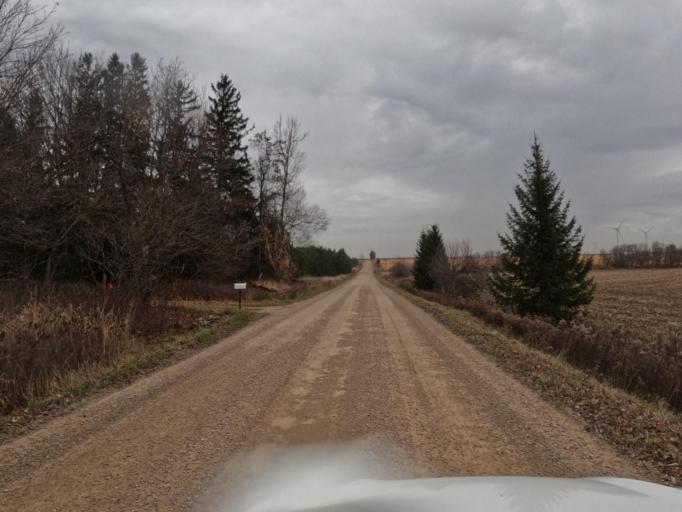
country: CA
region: Ontario
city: Shelburne
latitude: 43.8744
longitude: -80.3795
